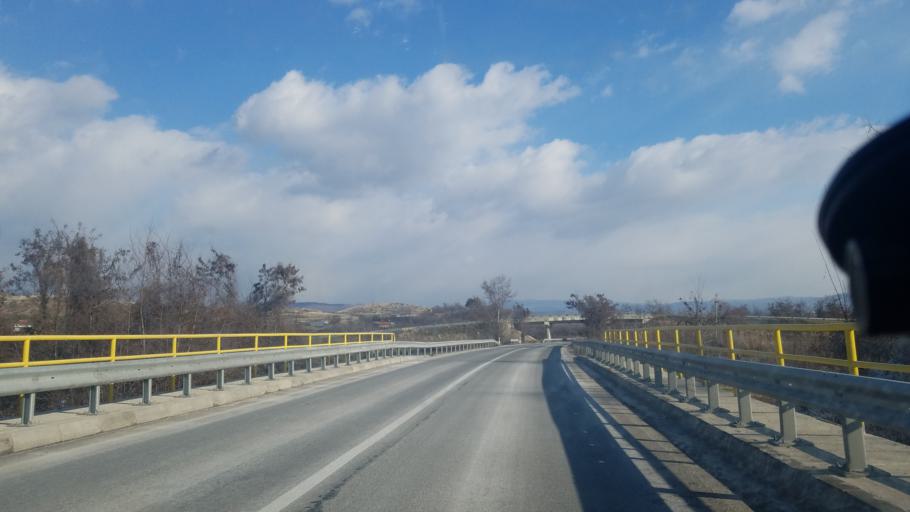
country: MK
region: Kocani
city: Orizari
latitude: 41.9111
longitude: 22.4431
